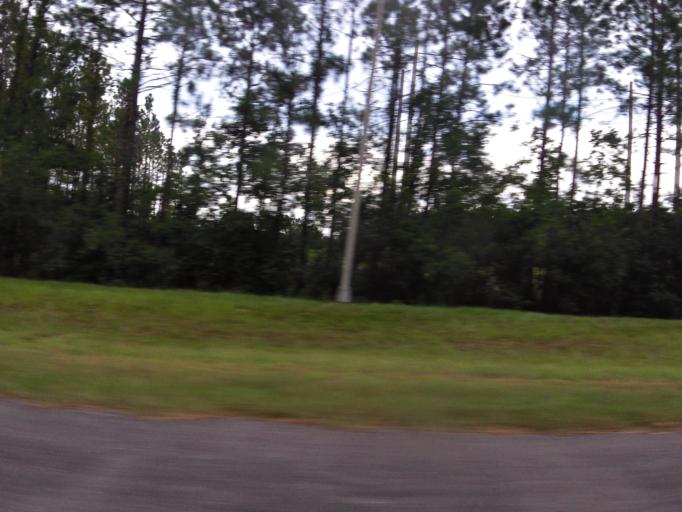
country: US
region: Florida
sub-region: Duval County
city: Baldwin
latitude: 30.3049
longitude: -81.8739
